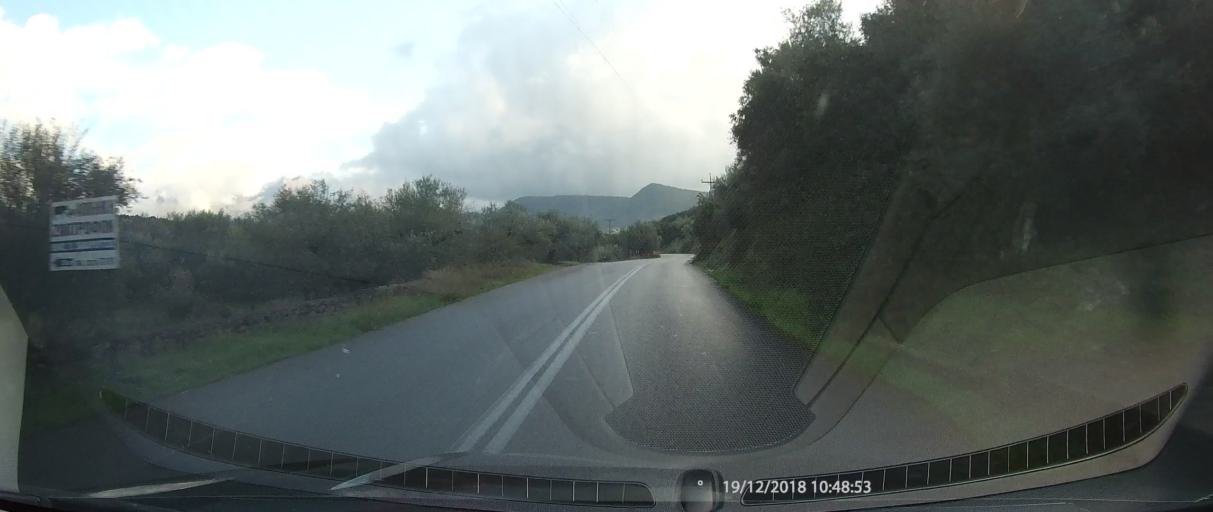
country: GR
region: Peloponnese
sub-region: Nomos Messinias
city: Kardamyli
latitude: 36.9297
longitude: 22.1921
